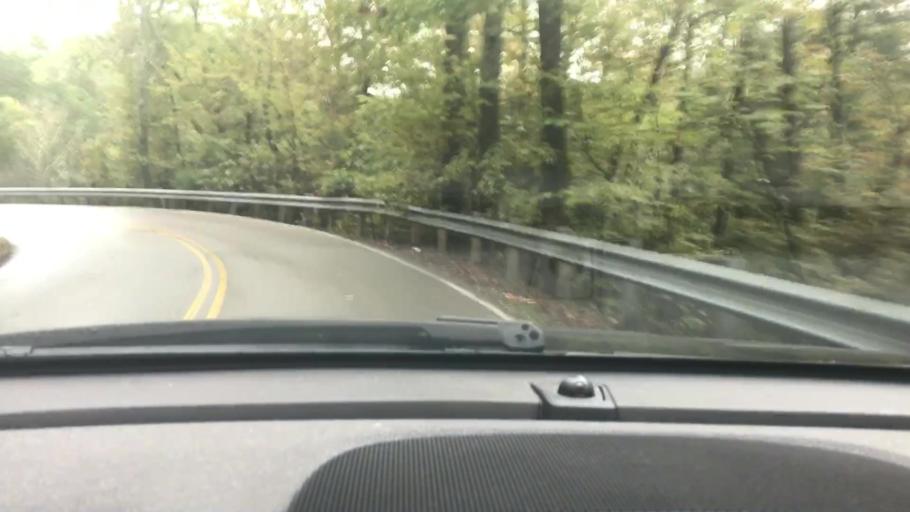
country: US
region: Tennessee
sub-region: Cheatham County
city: Kingston Springs
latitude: 36.1007
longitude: -87.1347
